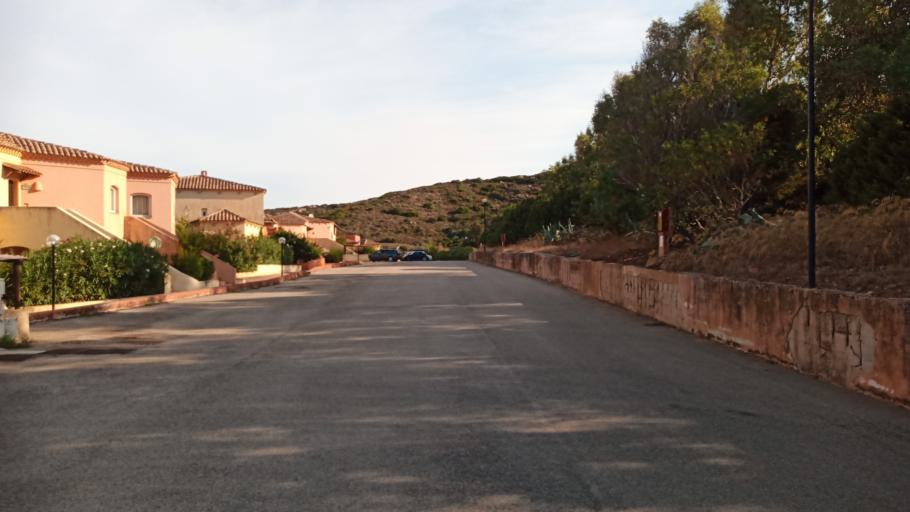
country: IT
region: Sardinia
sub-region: Provincia di Olbia-Tempio
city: Trinita d'Agultu
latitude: 41.0222
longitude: 8.8994
